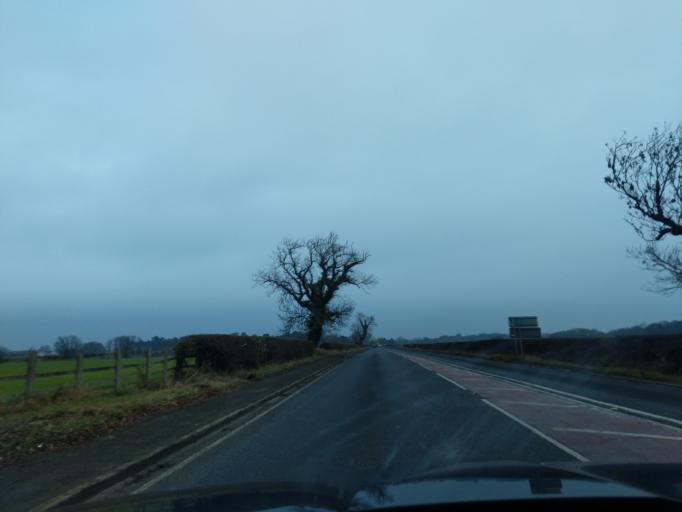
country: GB
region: England
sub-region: Northumberland
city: Stannington
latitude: 55.1373
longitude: -1.6496
